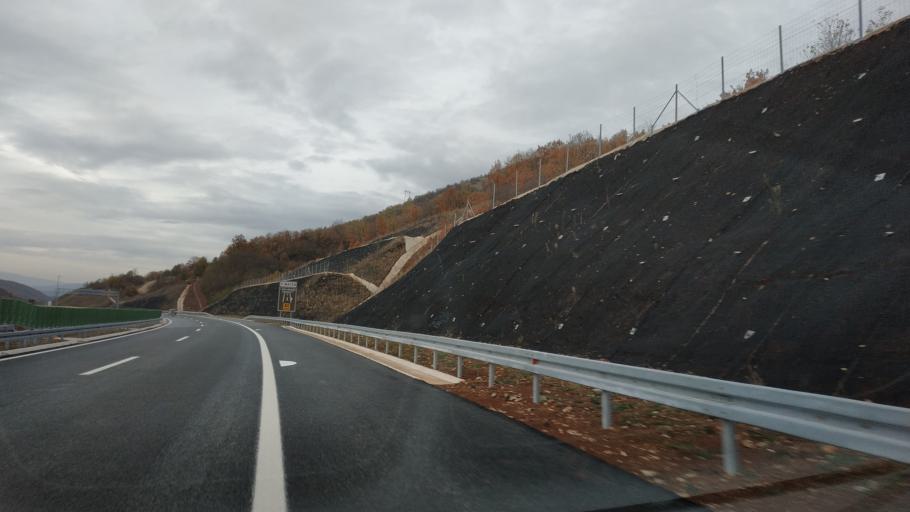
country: RS
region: Central Serbia
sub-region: Nisavski Okrug
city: Gadzin Han
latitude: 43.2804
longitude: 22.1350
